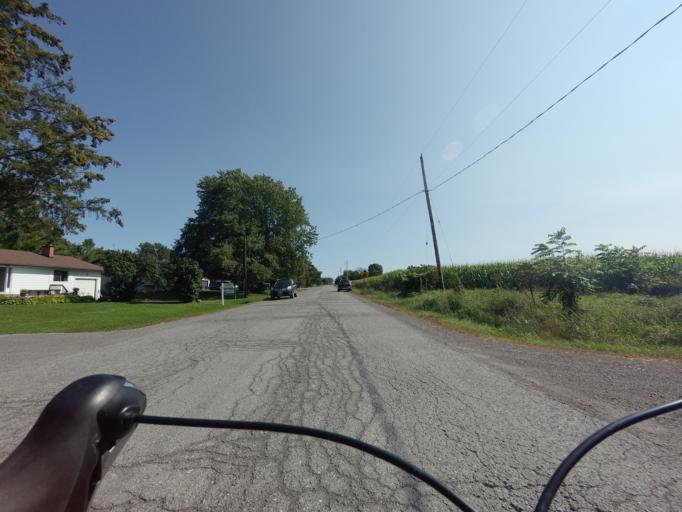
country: CA
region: Ontario
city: Carleton Place
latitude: 45.3591
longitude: -76.1234
